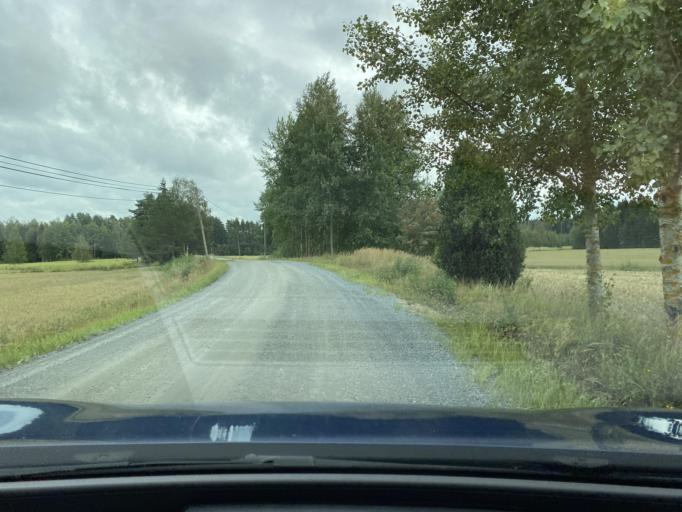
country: FI
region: Pirkanmaa
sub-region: Lounais-Pirkanmaa
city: Vammala
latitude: 61.2671
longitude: 22.9820
